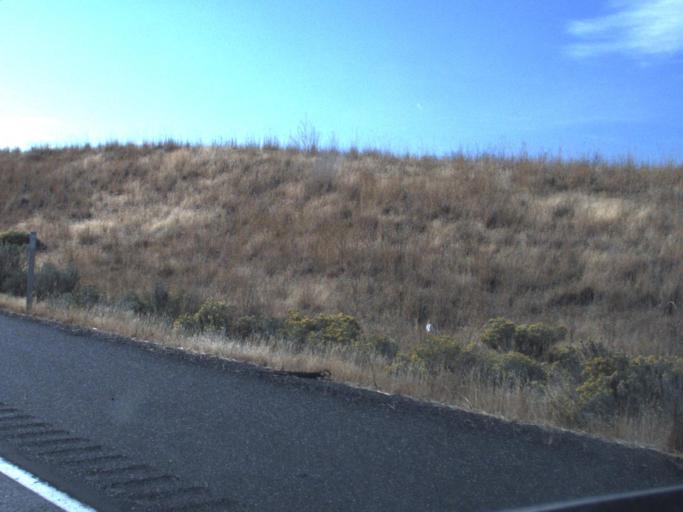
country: US
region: Oregon
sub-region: Umatilla County
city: Umatilla
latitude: 45.9829
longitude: -119.3209
